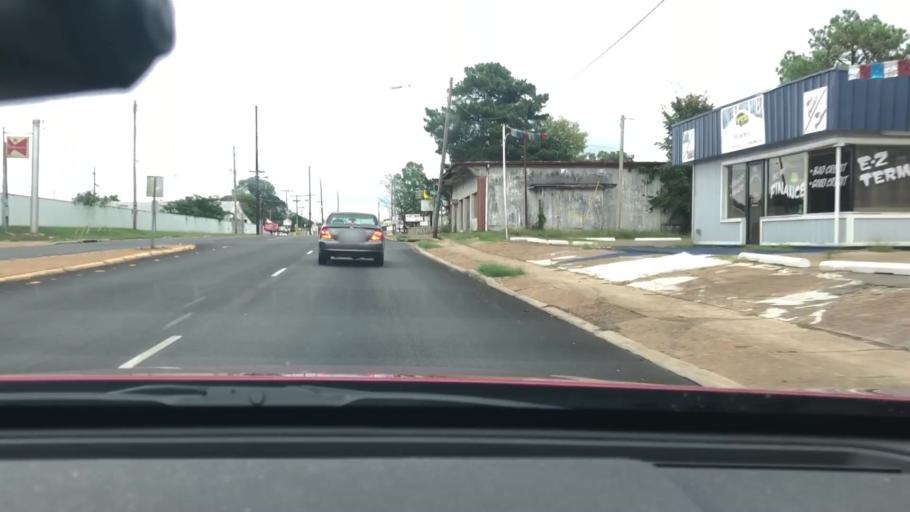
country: US
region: Arkansas
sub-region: Miller County
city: Texarkana
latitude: 33.4307
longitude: -94.0270
